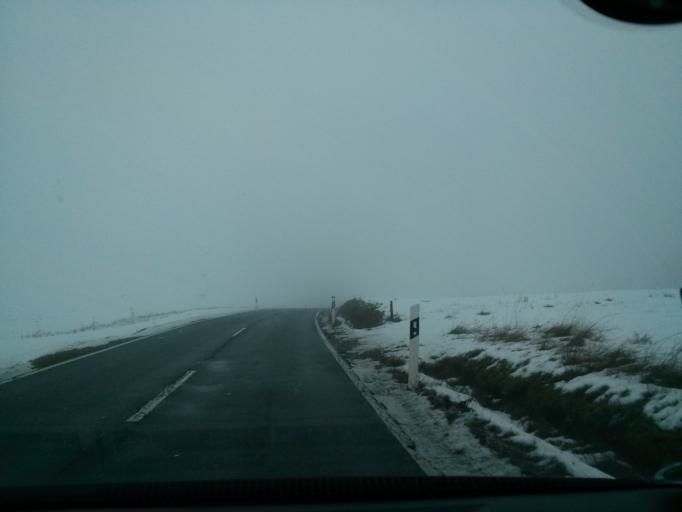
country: DE
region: Rheinland-Pfalz
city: Berg
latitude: 50.5691
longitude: 6.9525
